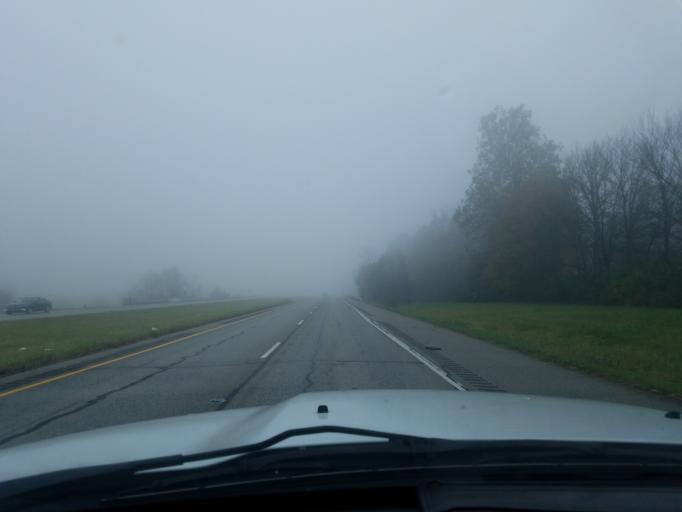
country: US
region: Indiana
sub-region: Floyd County
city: Galena
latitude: 38.3287
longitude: -85.8983
